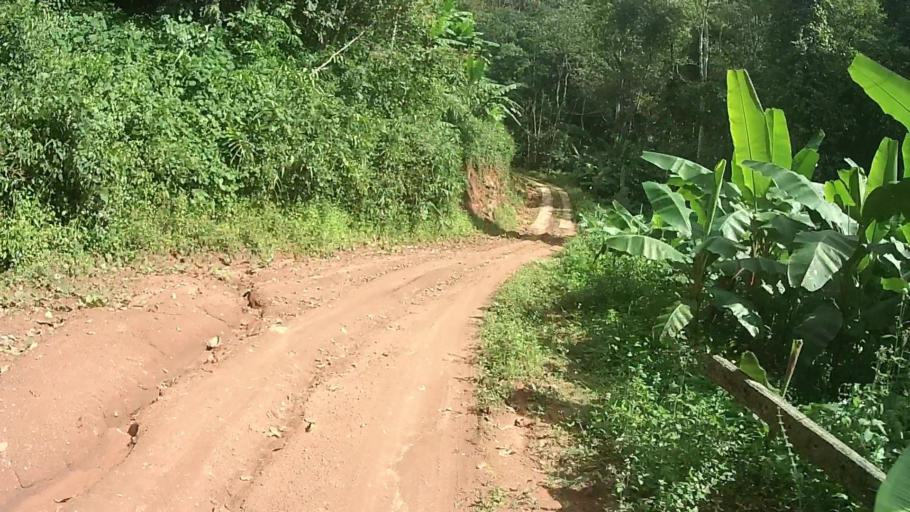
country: TH
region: Lampang
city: Mueang Pan
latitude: 18.9718
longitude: 99.4270
